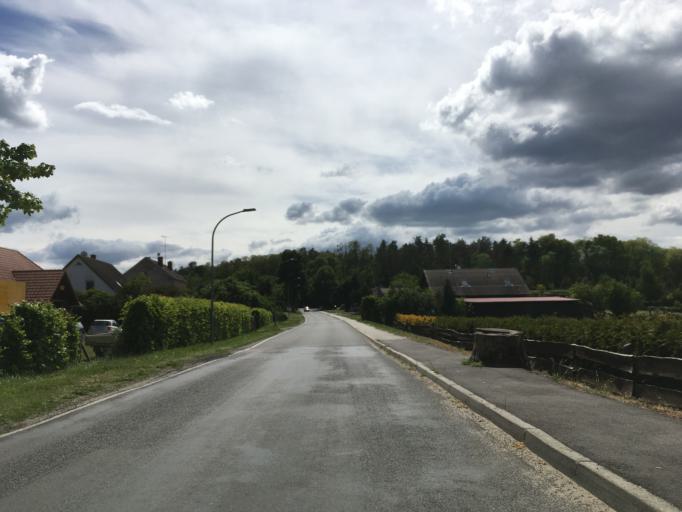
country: DE
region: Brandenburg
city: Protzel
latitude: 52.6849
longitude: 14.0091
